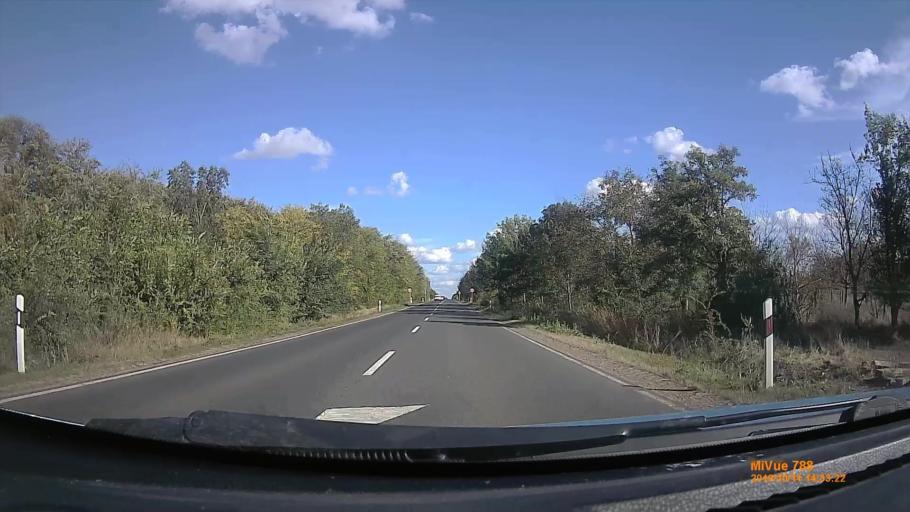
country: HU
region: Hajdu-Bihar
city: Ebes
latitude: 47.5619
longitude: 21.4549
